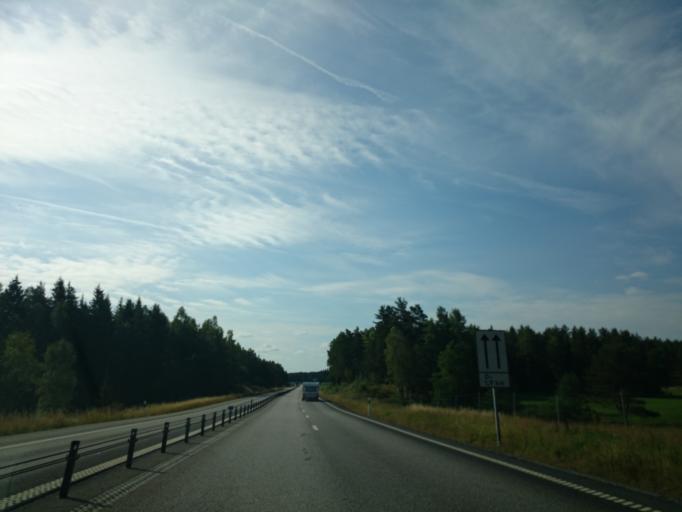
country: SE
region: OEstergoetland
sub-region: Valdemarsviks Kommun
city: Gusum
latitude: 58.2517
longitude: 16.5322
